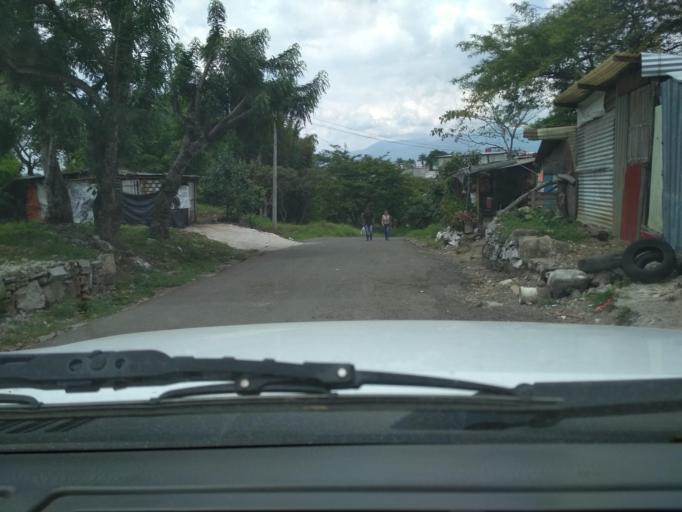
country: MX
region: Veracruz
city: Cordoba
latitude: 18.8883
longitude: -96.9202
